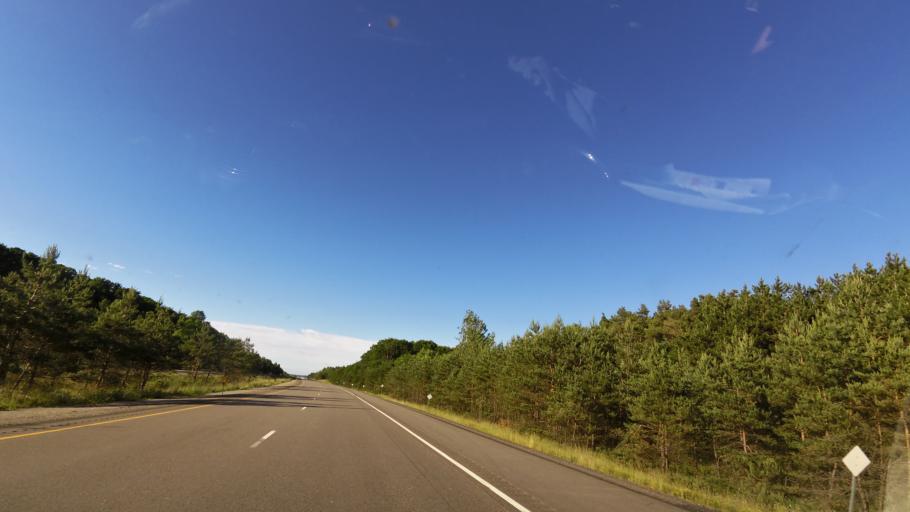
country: CA
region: Ontario
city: Barrie
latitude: 44.5977
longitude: -79.6767
